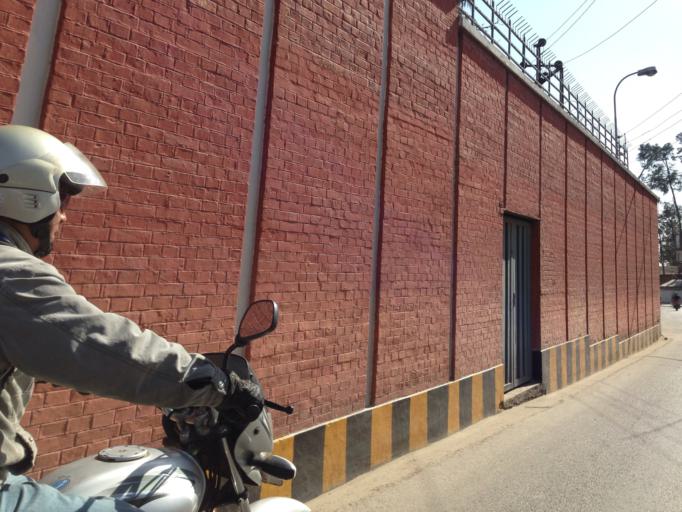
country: NP
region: Central Region
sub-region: Bagmati Zone
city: Kathmandu
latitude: 27.7274
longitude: 85.3306
